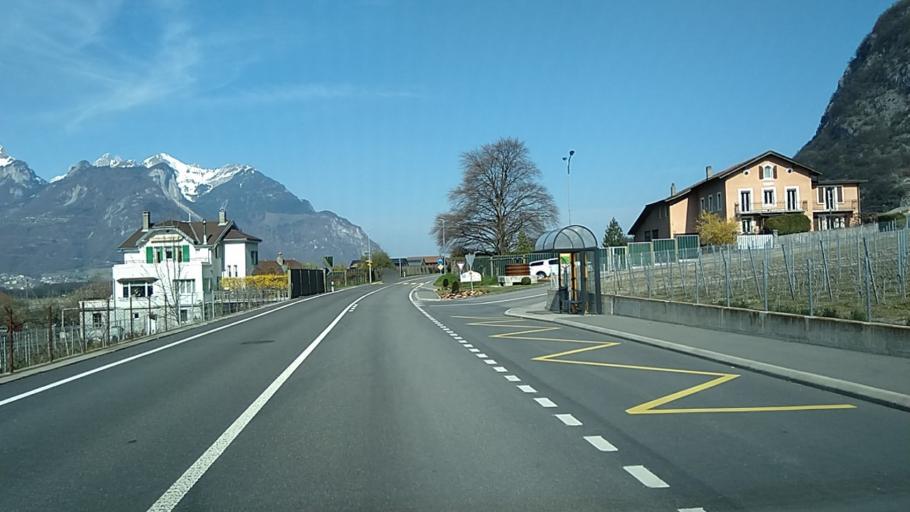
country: CH
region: Vaud
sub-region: Aigle District
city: Aigle
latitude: 46.3292
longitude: 6.9556
